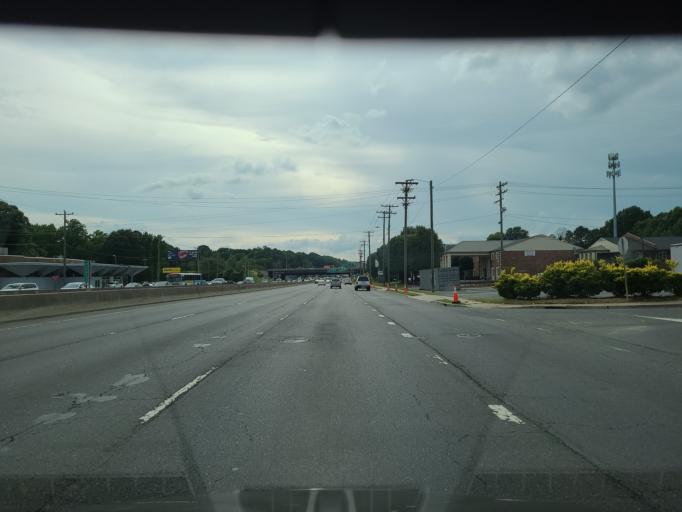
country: US
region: North Carolina
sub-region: Mecklenburg County
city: Charlotte
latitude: 35.2017
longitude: -80.7824
